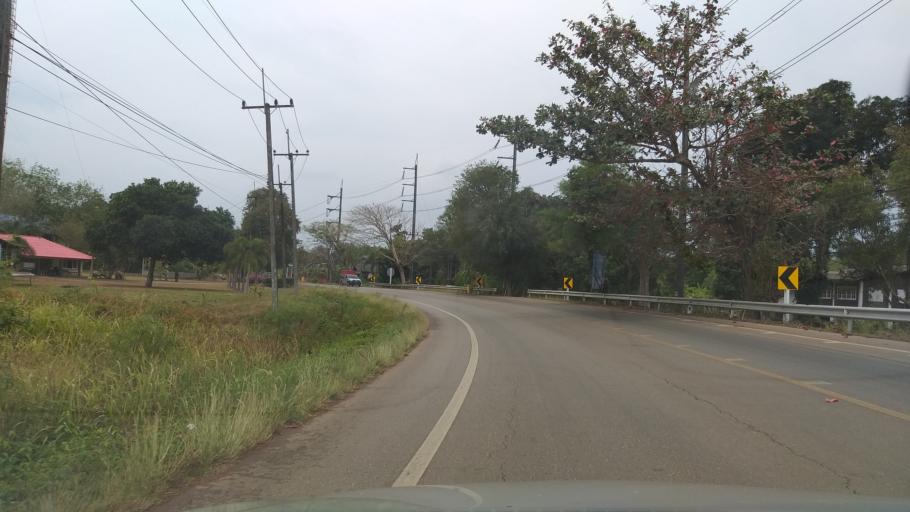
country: TH
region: Trat
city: Laem Ngop
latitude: 12.2316
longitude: 102.3047
